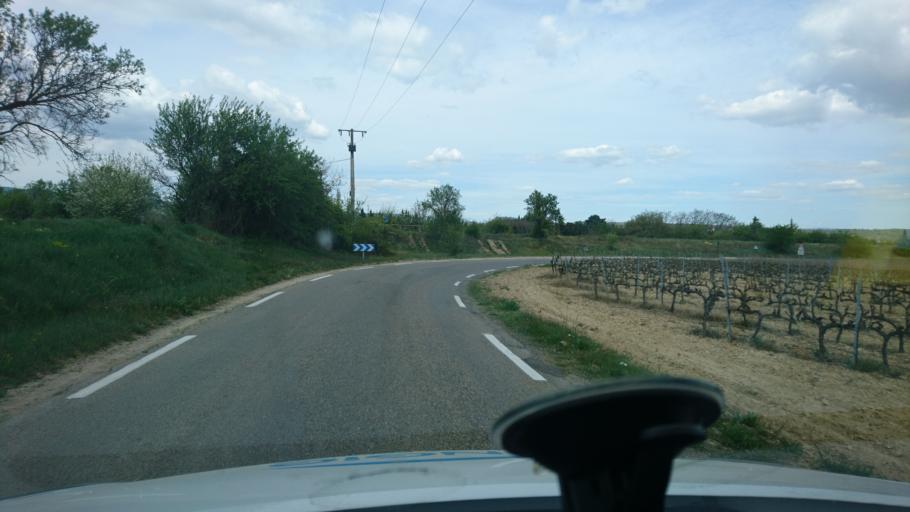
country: FR
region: Provence-Alpes-Cote d'Azur
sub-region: Departement du Vaucluse
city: Maubec
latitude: 43.8639
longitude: 5.1622
